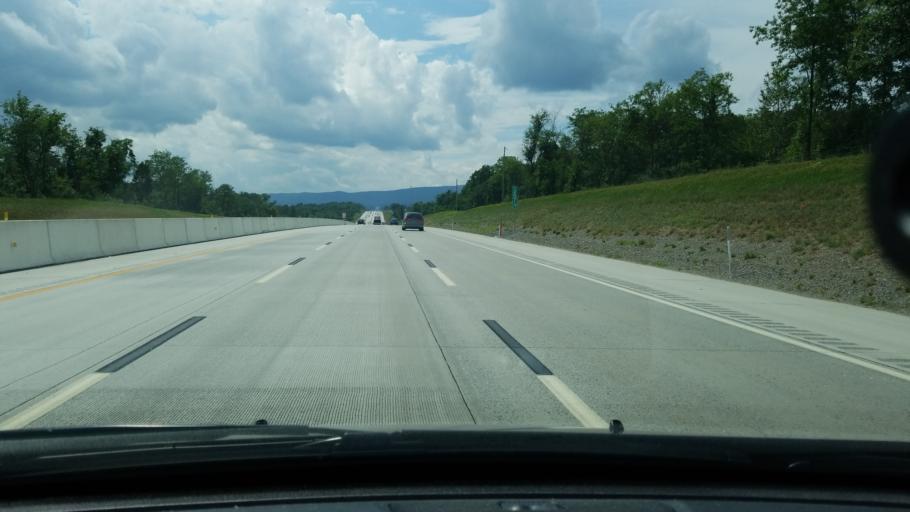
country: US
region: Pennsylvania
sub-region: Cumberland County
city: Newville
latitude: 40.1824
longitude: -77.4961
